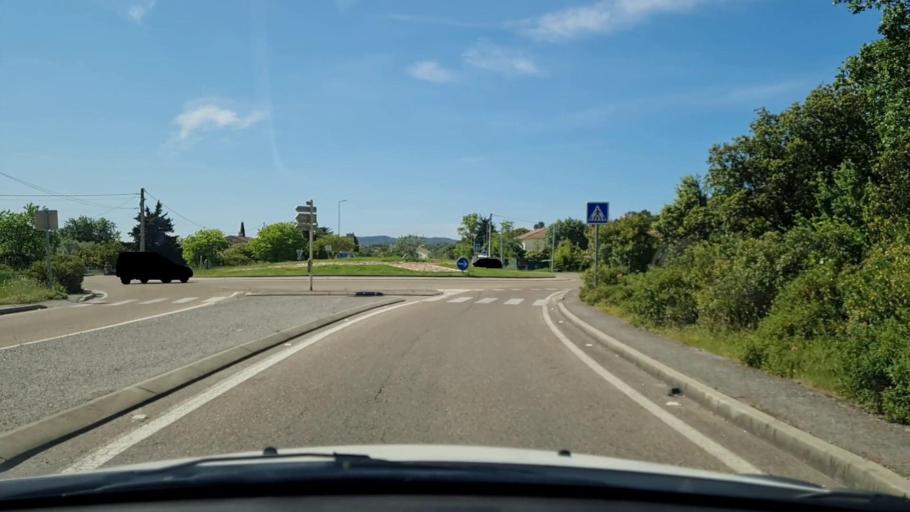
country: FR
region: Languedoc-Roussillon
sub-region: Departement du Gard
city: Vezenobres
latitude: 44.0433
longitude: 4.1459
